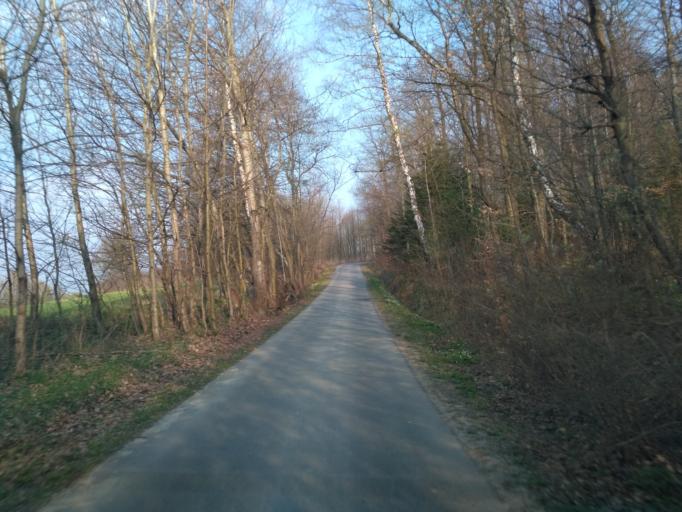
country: PL
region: Subcarpathian Voivodeship
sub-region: Powiat strzyzowski
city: Wisniowa
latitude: 49.8784
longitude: 21.6376
